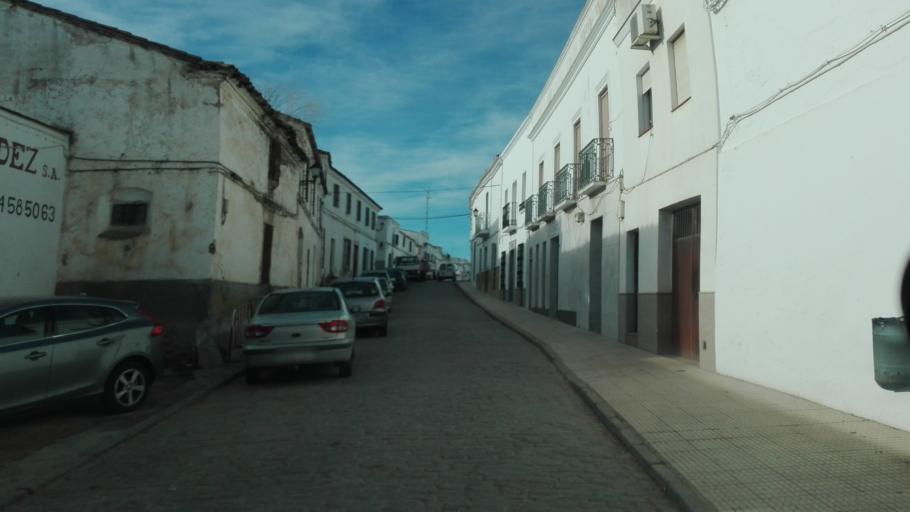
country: ES
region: Extremadura
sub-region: Provincia de Badajoz
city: Usagre
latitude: 38.3568
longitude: -6.1669
